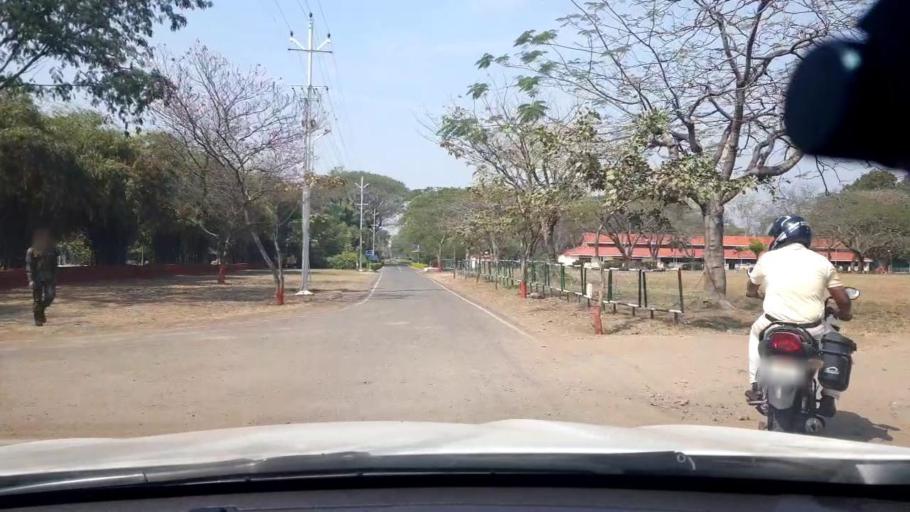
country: IN
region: Maharashtra
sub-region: Pune Division
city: Shivaji Nagar
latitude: 18.5442
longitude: 73.8652
